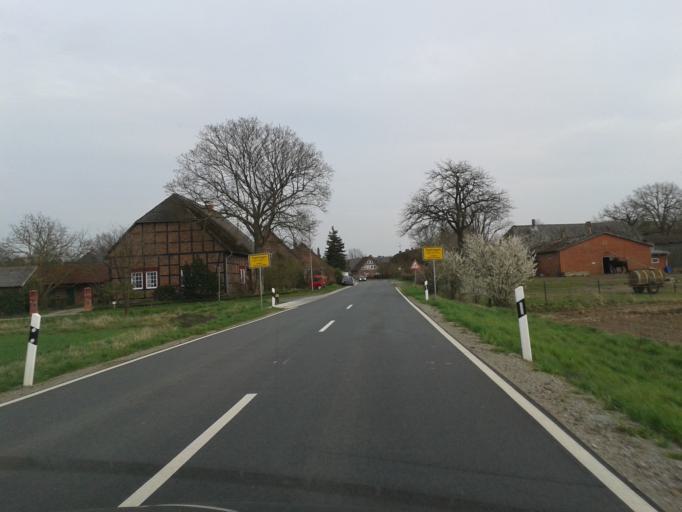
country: DE
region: Lower Saxony
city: Wustrow
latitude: 52.9168
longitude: 11.1495
